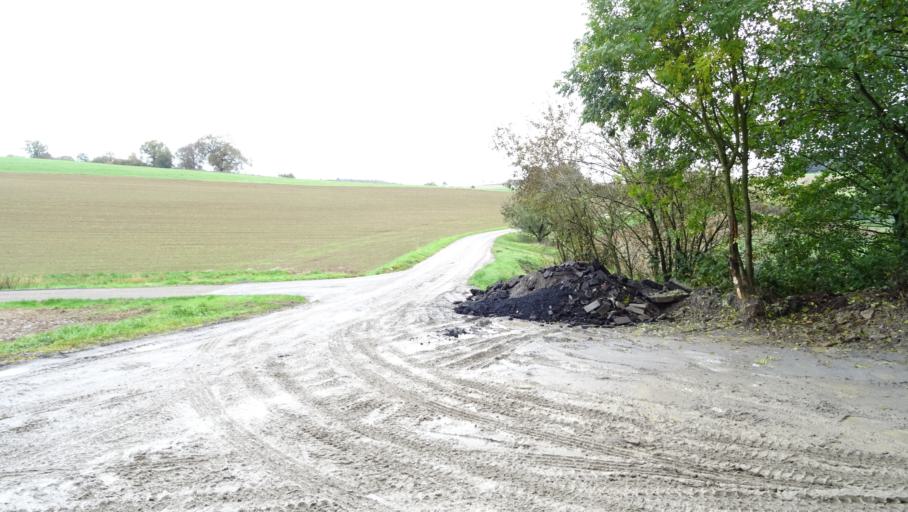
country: DE
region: Baden-Wuerttemberg
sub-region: Karlsruhe Region
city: Billigheim
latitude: 49.3405
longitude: 9.2216
